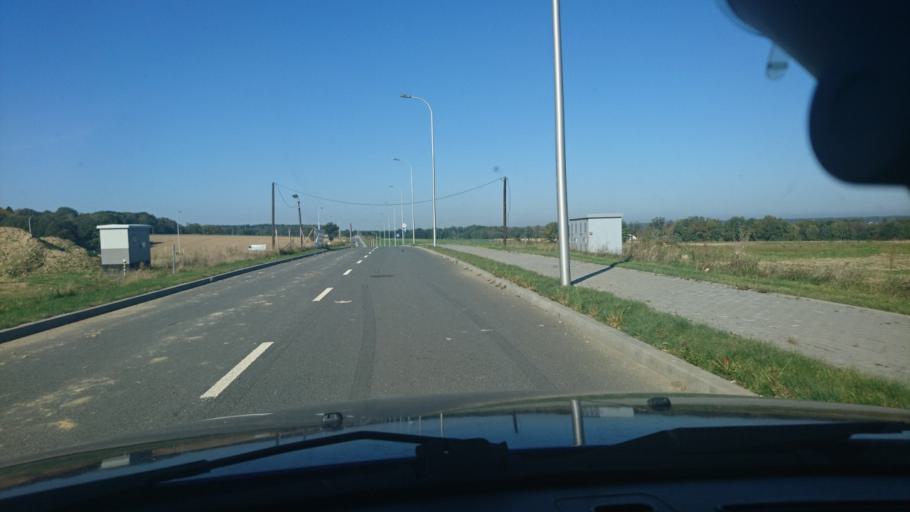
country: PL
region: Silesian Voivodeship
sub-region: Powiat bielski
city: Bronow
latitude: 49.8631
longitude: 18.9342
